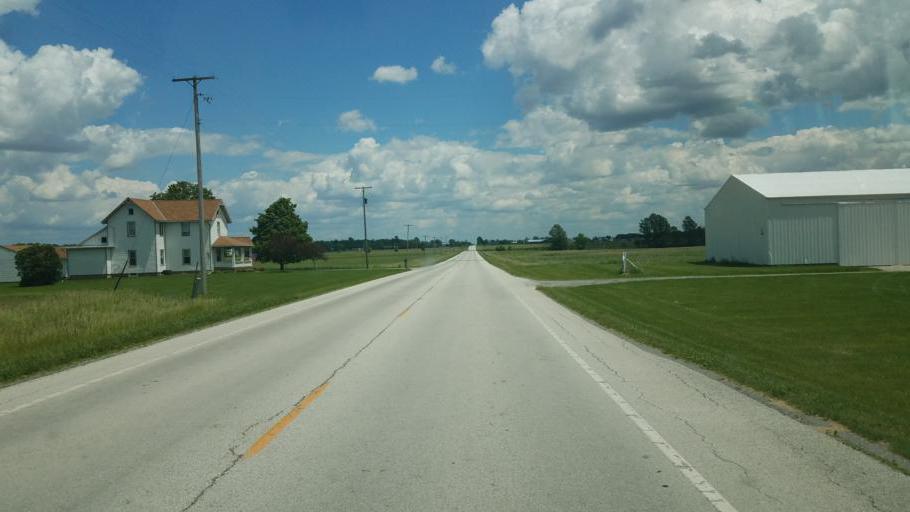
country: US
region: Ohio
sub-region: Wyandot County
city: Upper Sandusky
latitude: 40.8406
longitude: -83.1794
